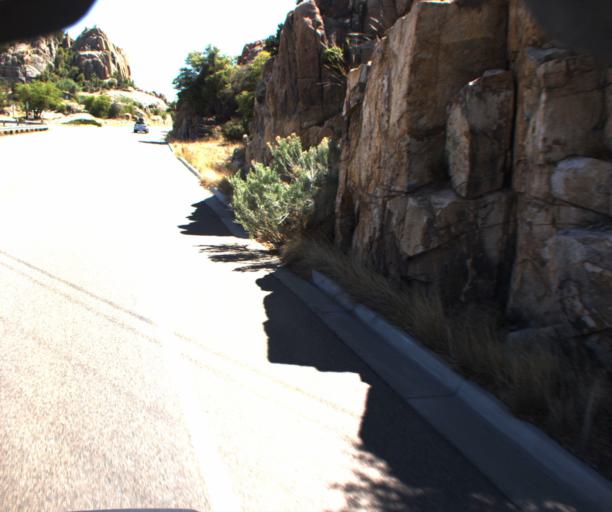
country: US
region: Arizona
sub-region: Yavapai County
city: Prescott
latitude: 34.6114
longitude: -112.4191
